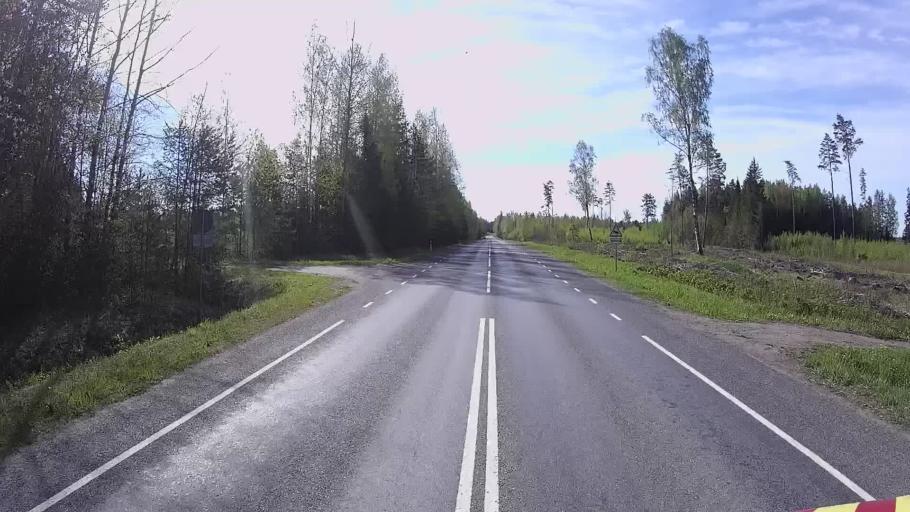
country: EE
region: Polvamaa
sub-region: Polva linn
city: Polva
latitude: 58.1817
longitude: 27.1080
